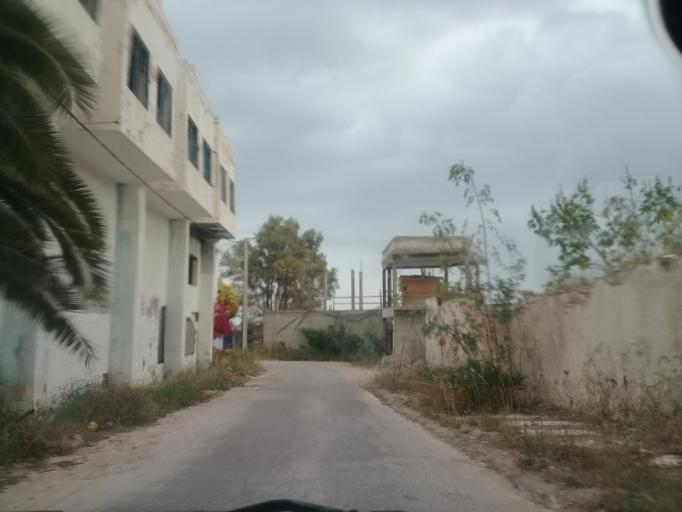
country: TN
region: Tunis
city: Sidi Bou Said
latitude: 36.8646
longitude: 10.3421
